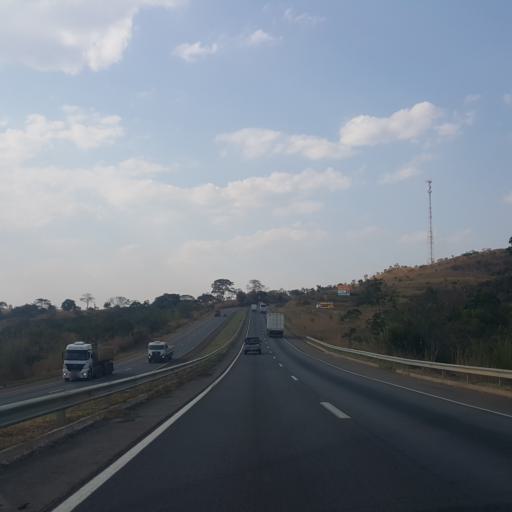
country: BR
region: Goias
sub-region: Abadiania
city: Abadiania
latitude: -16.1031
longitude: -48.5237
